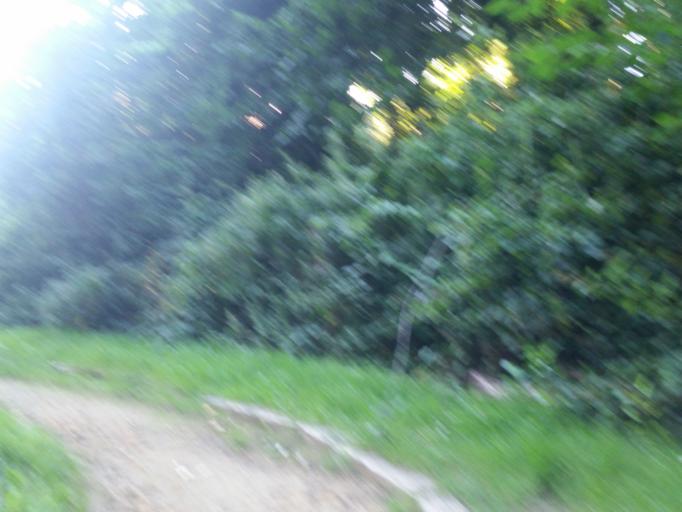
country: GB
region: England
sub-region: East Sussex
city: Hastings
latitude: 50.8613
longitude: 0.5944
